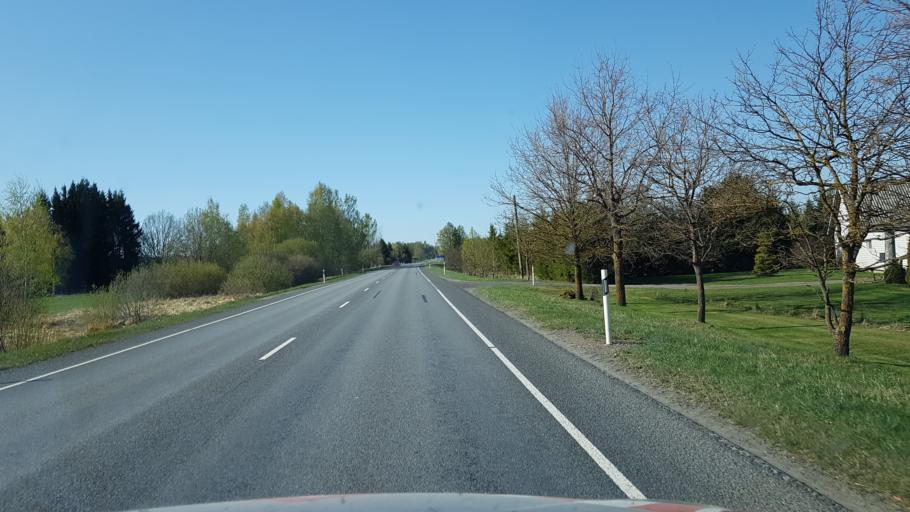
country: EE
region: Paernumaa
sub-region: Paikuse vald
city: Paikuse
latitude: 58.2318
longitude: 24.6982
